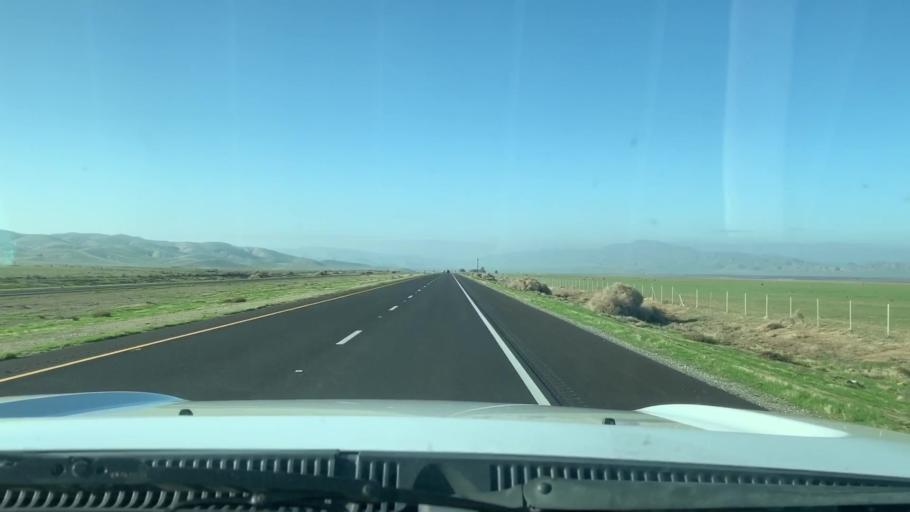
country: US
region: California
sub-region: Kern County
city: Lost Hills
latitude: 35.6285
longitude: -119.9936
